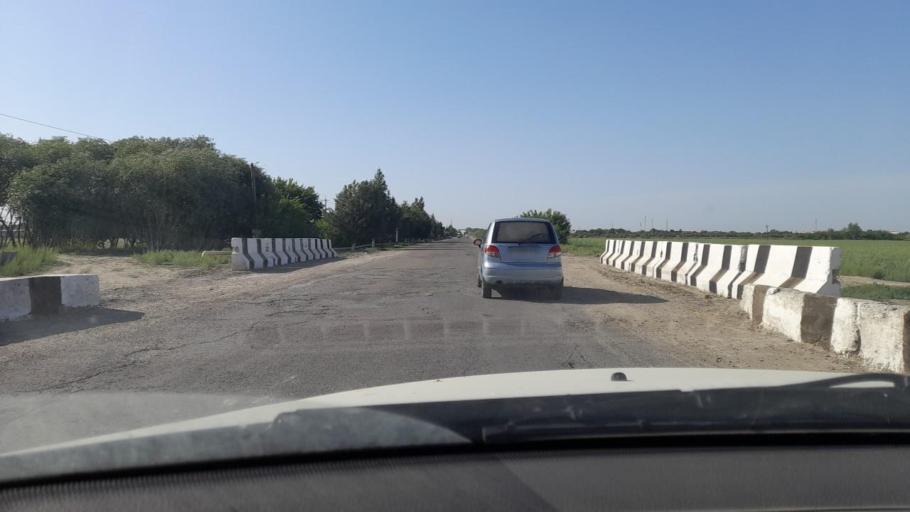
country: UZ
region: Bukhara
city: Romiton
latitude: 40.0720
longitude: 64.3265
